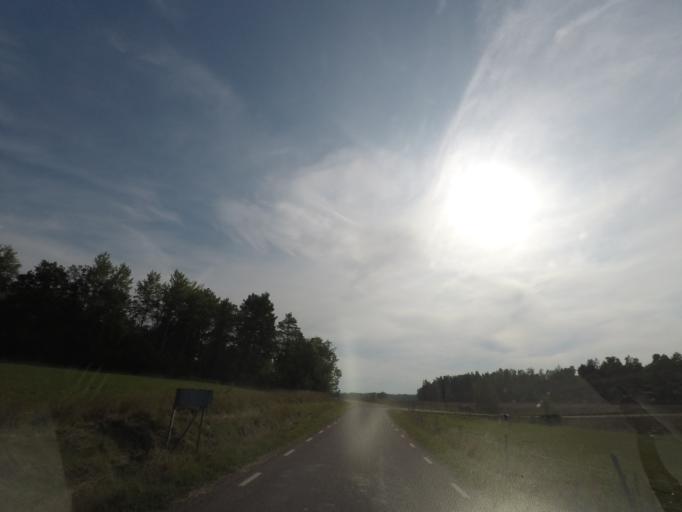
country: SE
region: Vaestmanland
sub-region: Kungsors Kommun
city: Kungsoer
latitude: 59.5003
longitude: 16.1536
